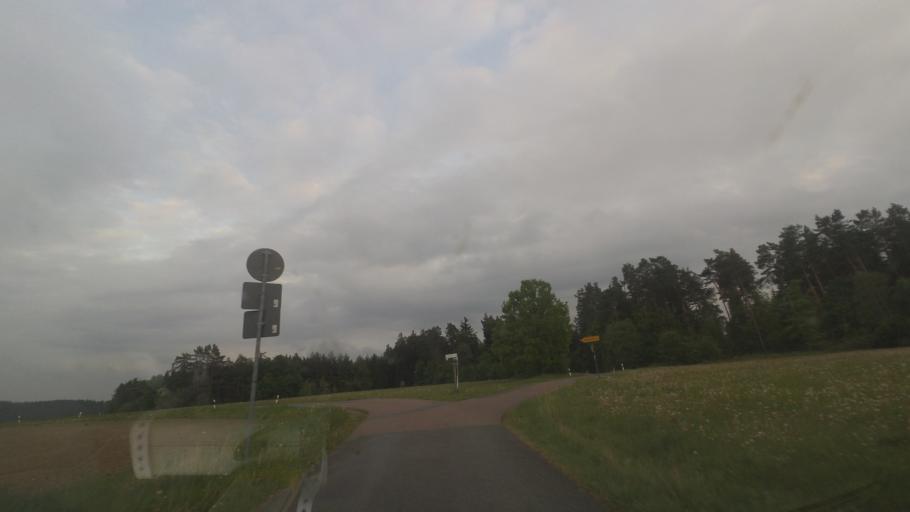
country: DE
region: Thuringia
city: Konigsee
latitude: 50.7189
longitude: 11.1033
